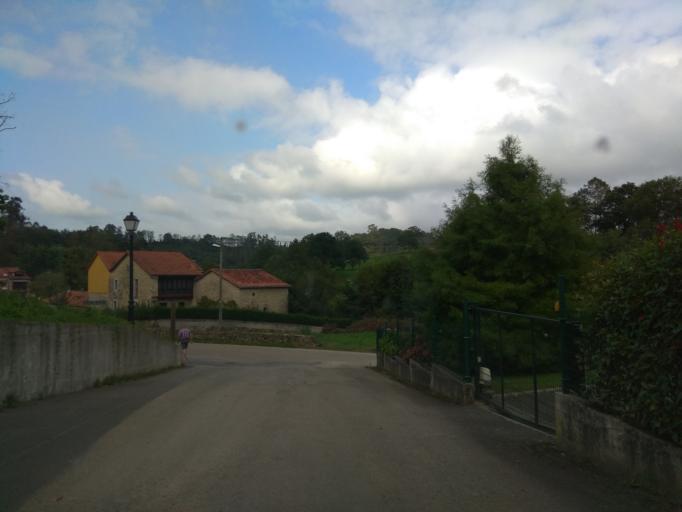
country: ES
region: Cantabria
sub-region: Provincia de Cantabria
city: San Vicente de la Barquera
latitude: 43.3181
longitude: -4.3520
